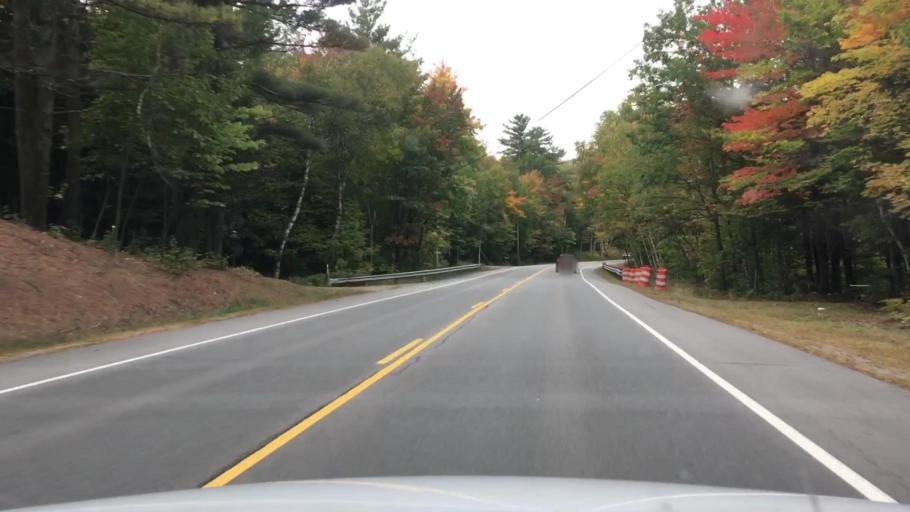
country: US
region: New Hampshire
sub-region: Coos County
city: Gorham
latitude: 44.3910
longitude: -71.1269
